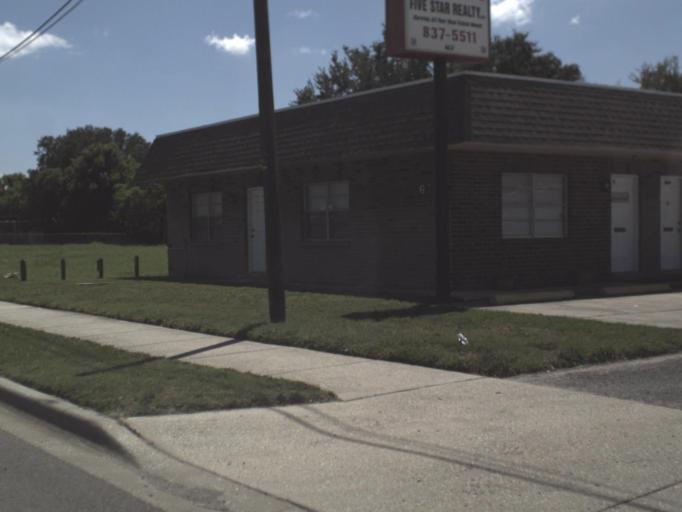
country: US
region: Florida
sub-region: Hillsborough County
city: Tampa
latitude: 27.8789
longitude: -82.5066
